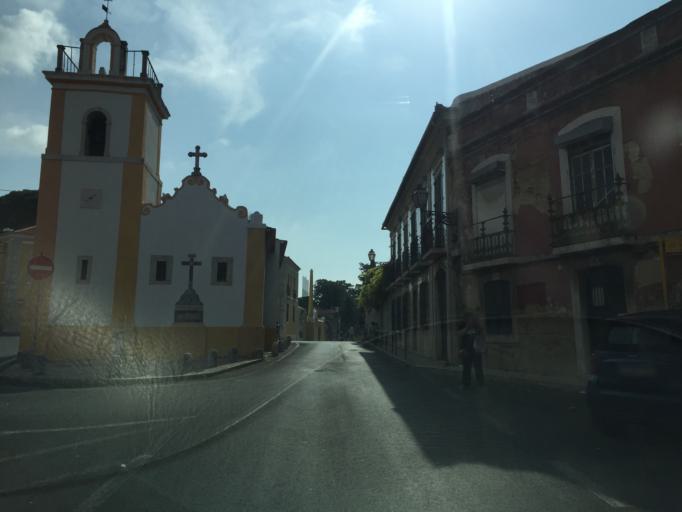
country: PT
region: Lisbon
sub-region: Odivelas
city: Olival do Basto
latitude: 38.7723
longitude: -9.1736
